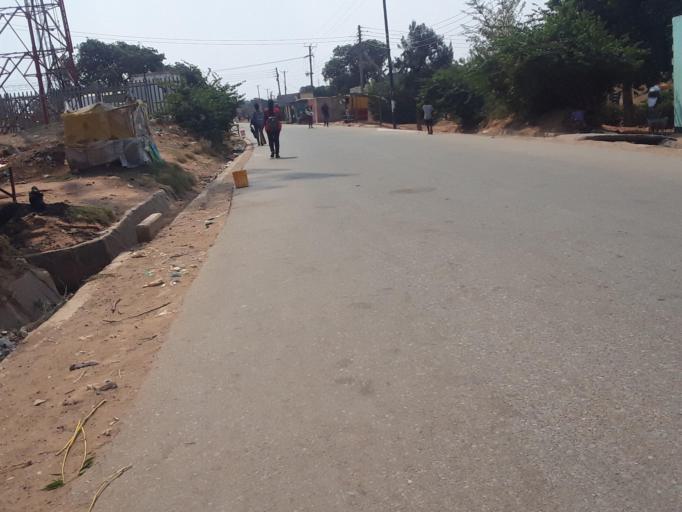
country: ZM
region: Lusaka
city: Lusaka
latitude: -15.3588
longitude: 28.2991
